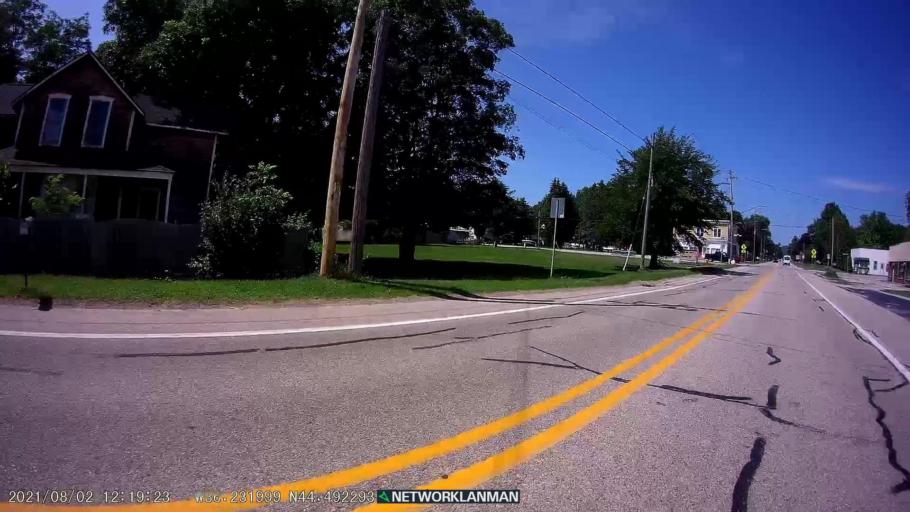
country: US
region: Michigan
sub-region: Benzie County
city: Frankfort
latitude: 44.4925
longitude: -86.2317
